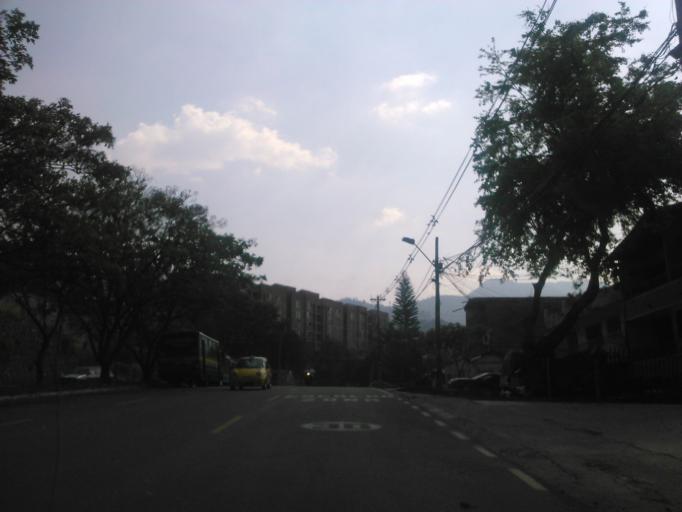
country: CO
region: Antioquia
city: Medellin
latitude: 6.2548
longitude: -75.6145
